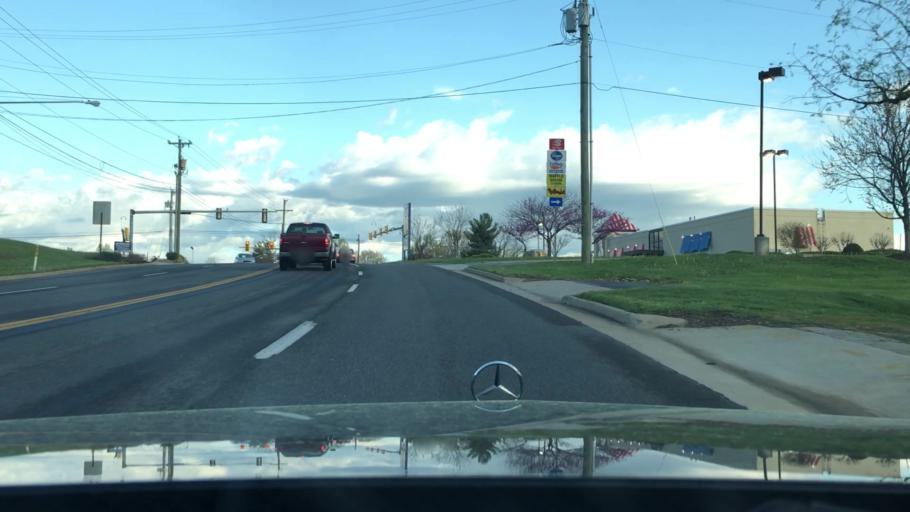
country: US
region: Virginia
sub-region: Campbell County
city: Timberlake
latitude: 37.3437
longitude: -79.2334
